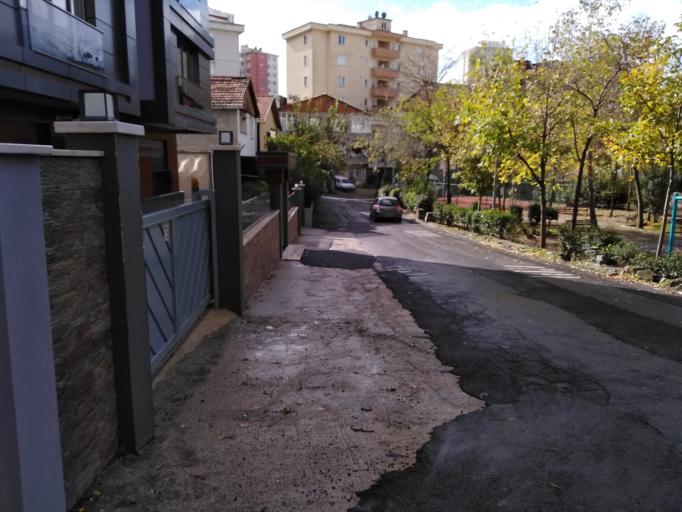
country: TR
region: Istanbul
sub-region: Atasehir
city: Atasehir
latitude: 40.9813
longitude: 29.1218
